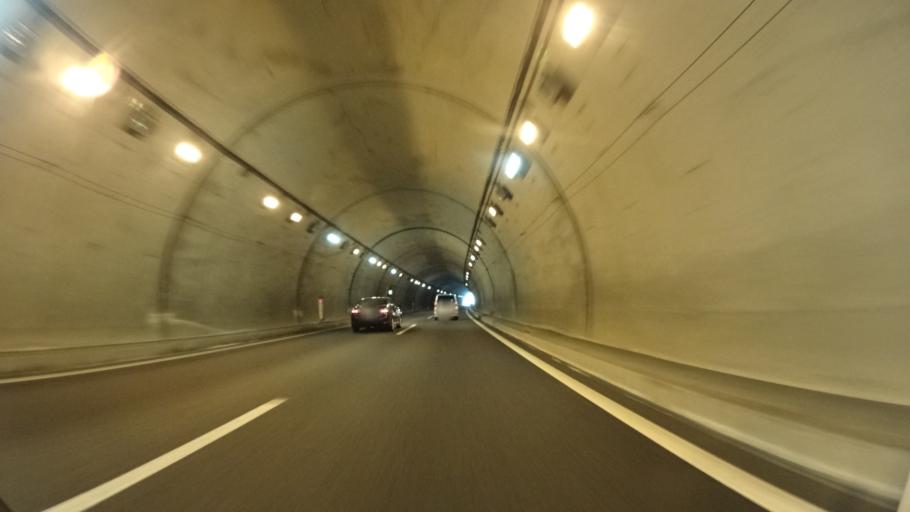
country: JP
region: Ehime
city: Saijo
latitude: 33.8866
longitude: 133.1757
